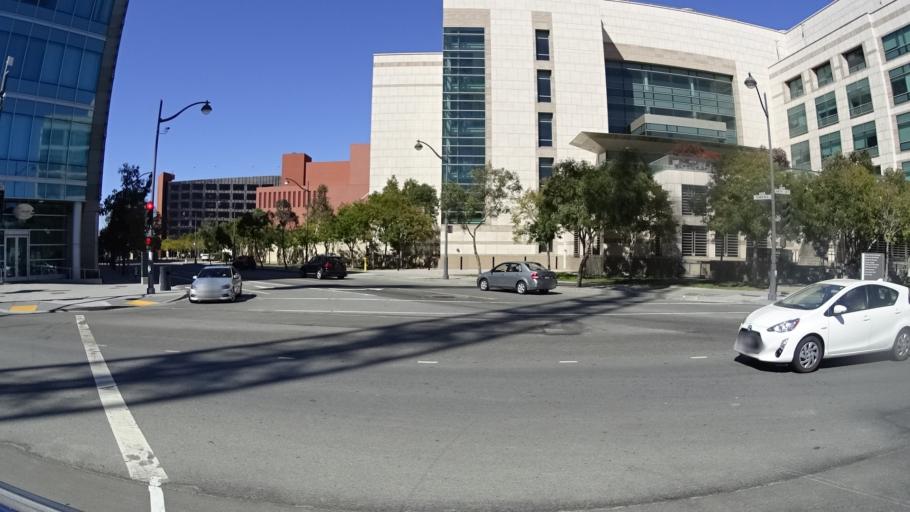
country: US
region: California
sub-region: San Francisco County
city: San Francisco
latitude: 37.7667
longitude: -122.3928
